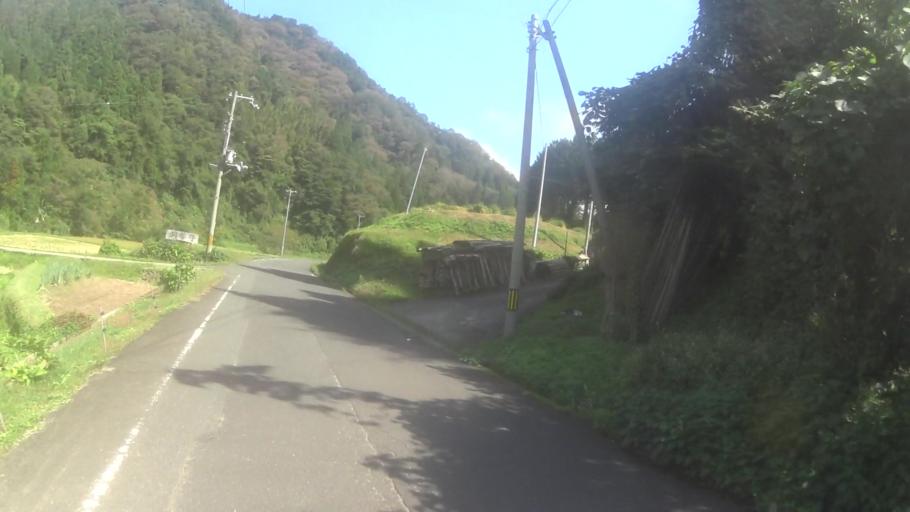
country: JP
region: Kyoto
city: Miyazu
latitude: 35.6801
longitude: 135.1616
